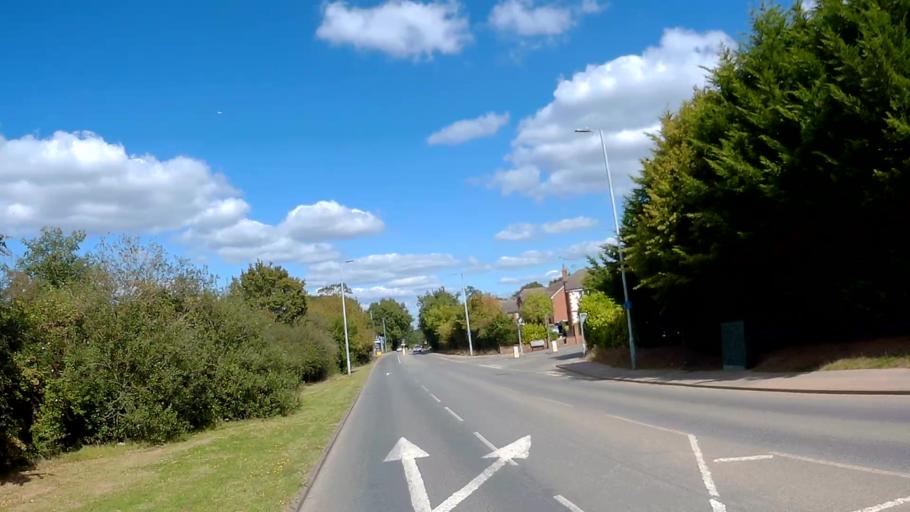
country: GB
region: England
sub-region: Bracknell Forest
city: Binfield
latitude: 51.4236
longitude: -0.7774
